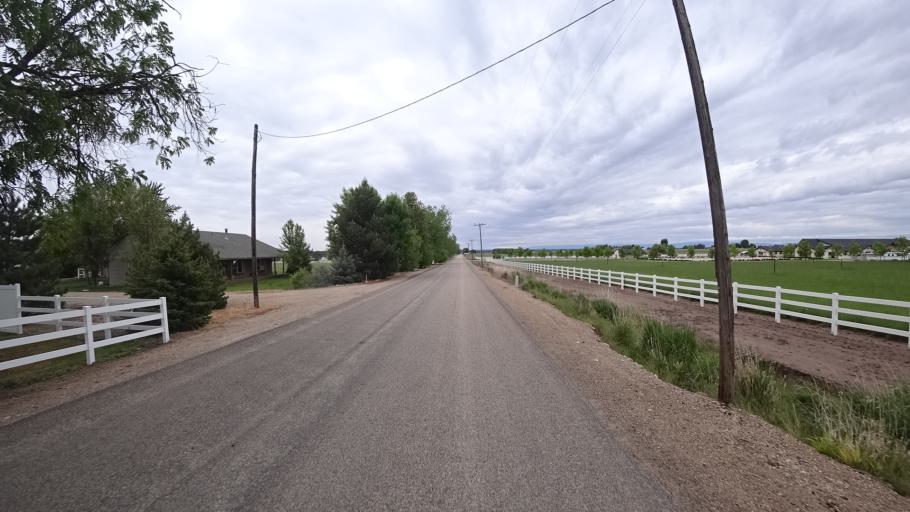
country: US
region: Idaho
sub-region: Ada County
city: Eagle
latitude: 43.7311
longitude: -116.4134
